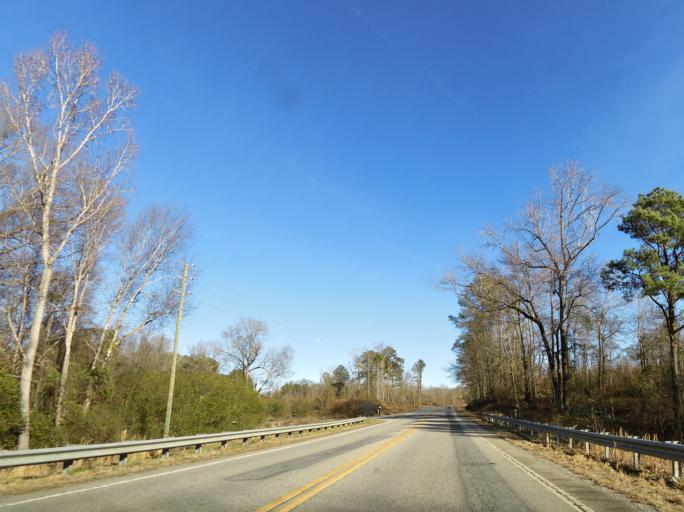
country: US
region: Georgia
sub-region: Crawford County
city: Knoxville
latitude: 32.7239
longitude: -83.9889
